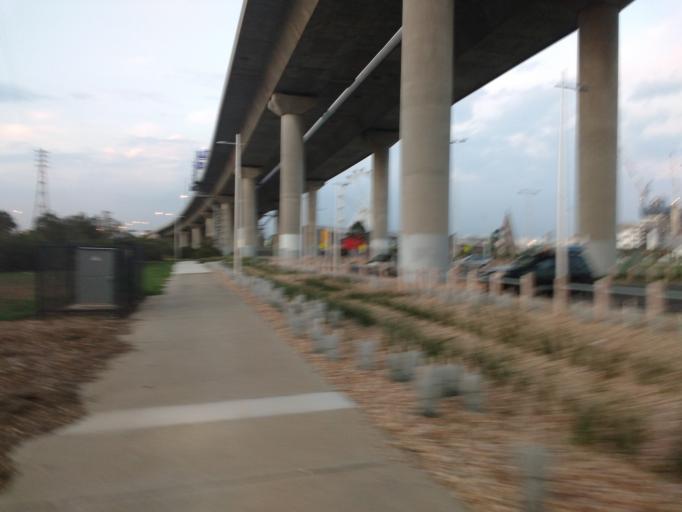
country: AU
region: Victoria
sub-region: Melbourne
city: Docklands
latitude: -37.8172
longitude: 144.9329
